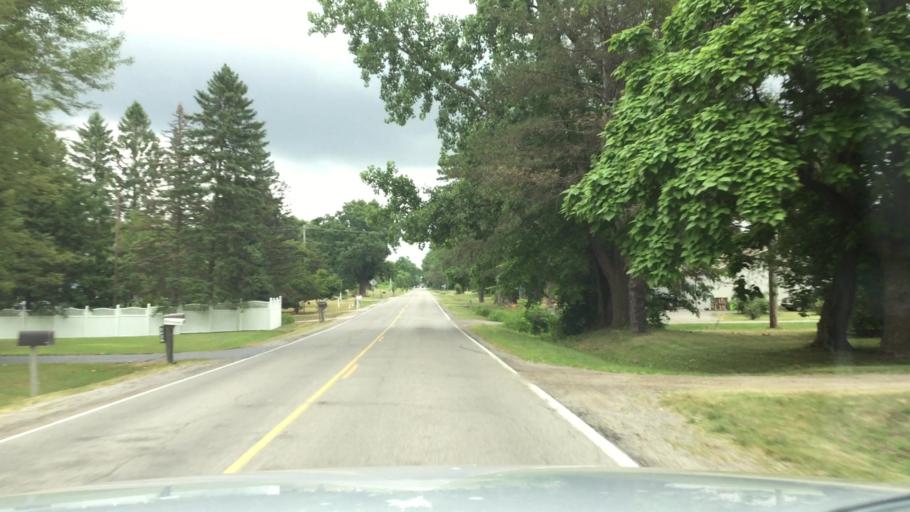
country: US
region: Michigan
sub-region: Genesee County
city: Clio
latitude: 43.1627
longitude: -83.7907
